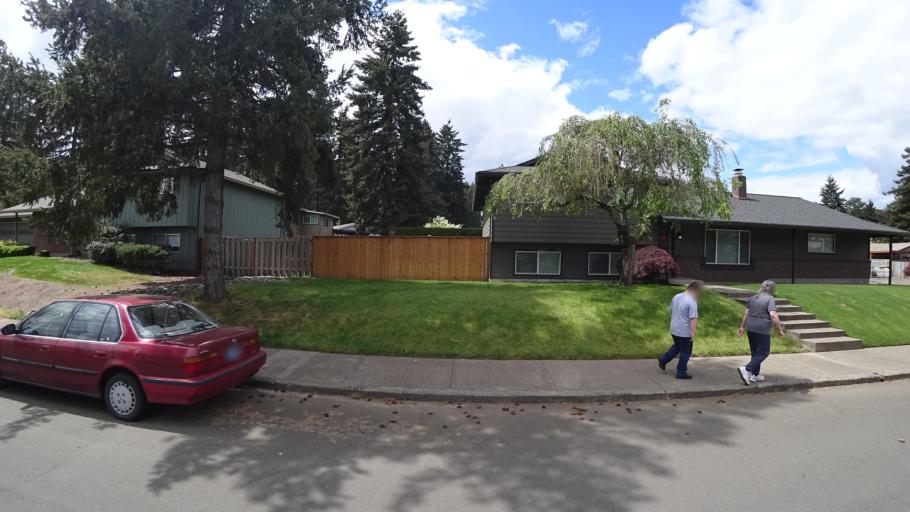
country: US
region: Oregon
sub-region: Washington County
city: Aloha
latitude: 45.4723
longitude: -122.8551
